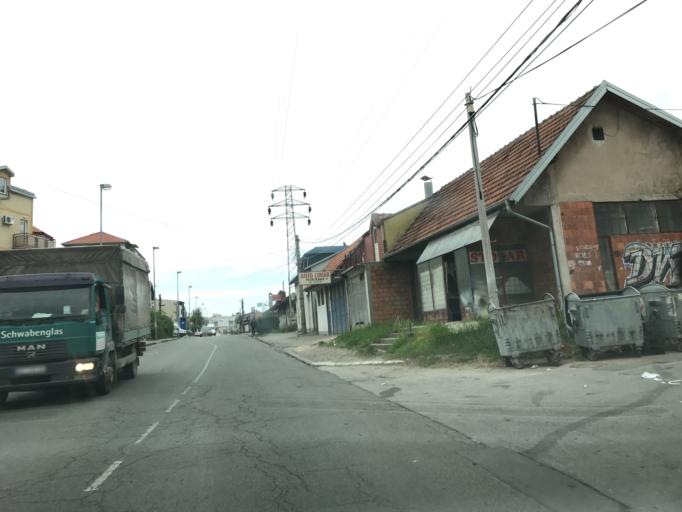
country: RS
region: Central Serbia
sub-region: Belgrade
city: Palilula
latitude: 44.7964
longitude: 20.5222
